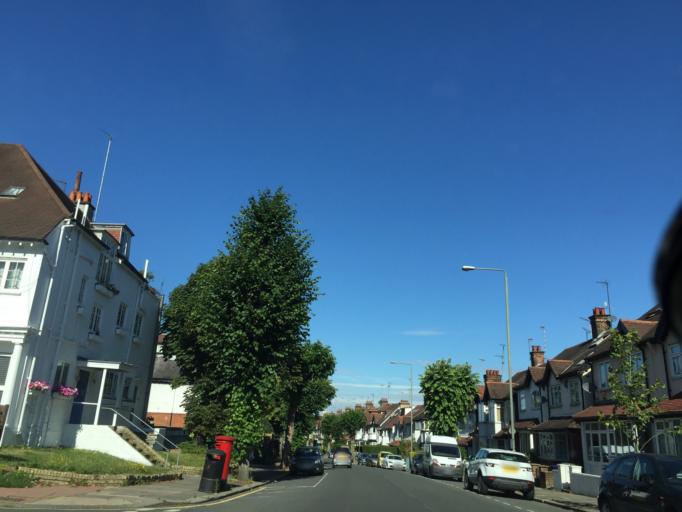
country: GB
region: England
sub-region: Greater London
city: Belsize Park
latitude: 51.5707
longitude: -0.1890
